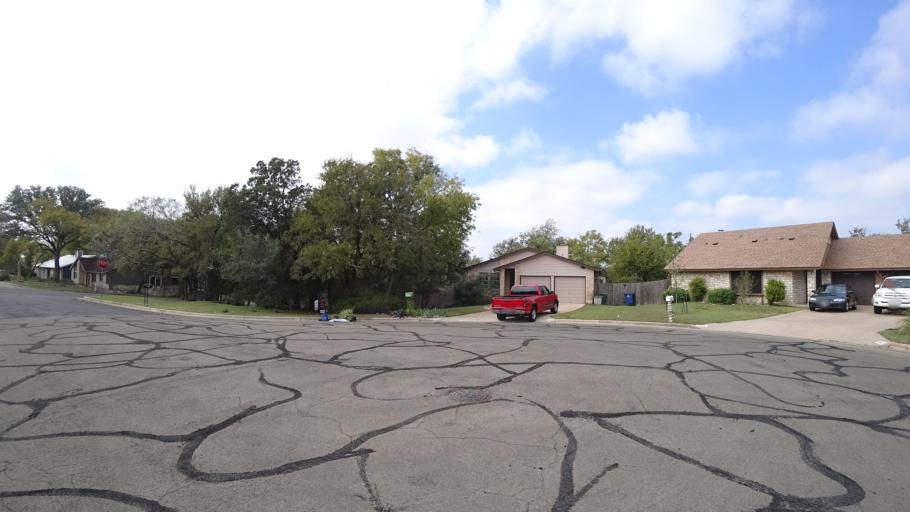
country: US
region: Texas
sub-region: Travis County
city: Shady Hollow
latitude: 30.1991
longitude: -97.8312
